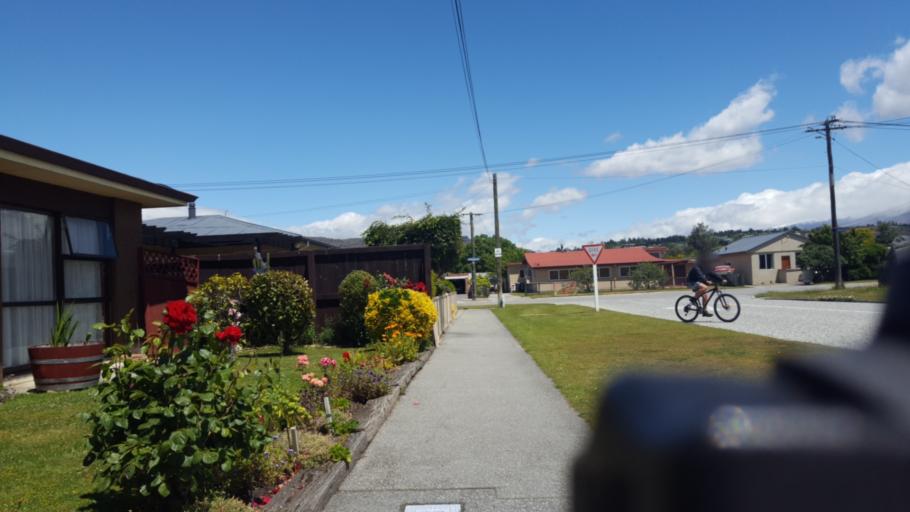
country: NZ
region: Otago
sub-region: Queenstown-Lakes District
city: Wanaka
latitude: -45.2482
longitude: 169.3908
